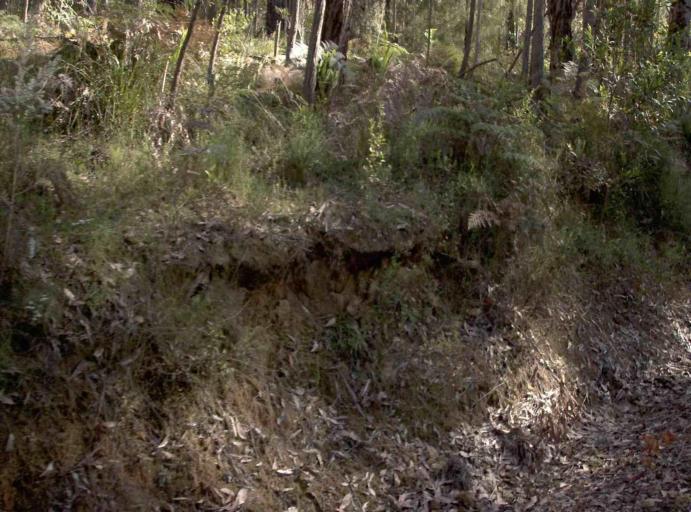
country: AU
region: Victoria
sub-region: East Gippsland
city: Lakes Entrance
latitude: -37.6226
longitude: 148.5100
